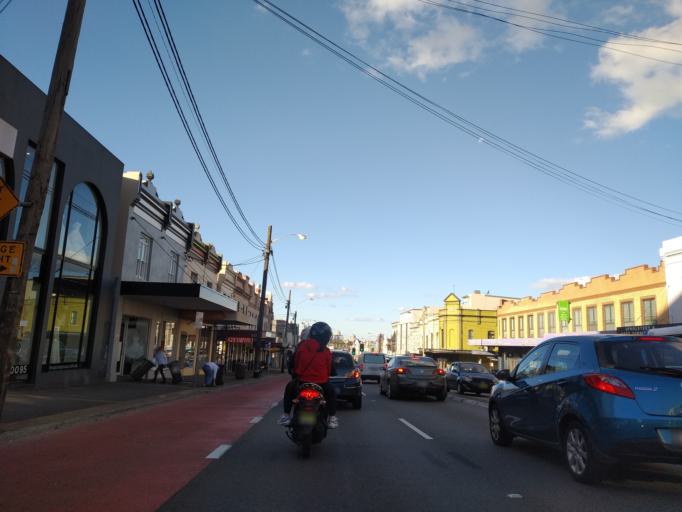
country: AU
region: New South Wales
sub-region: Marrickville
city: Lewisham
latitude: -33.8886
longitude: 151.1559
